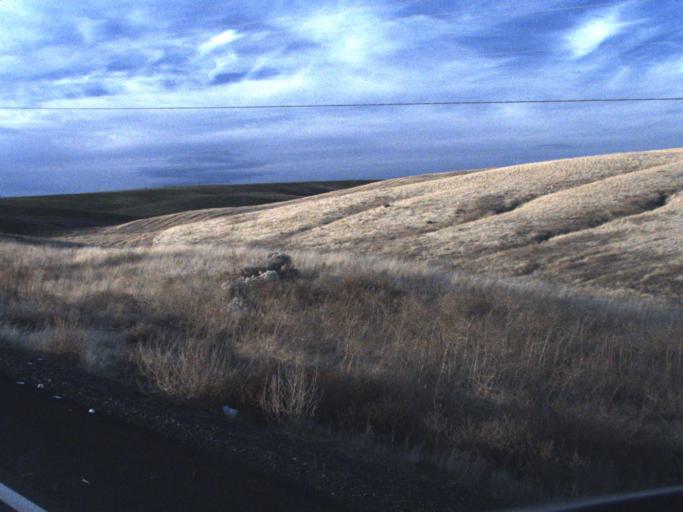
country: US
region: Washington
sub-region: Walla Walla County
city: Burbank
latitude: 46.0583
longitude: -118.7290
